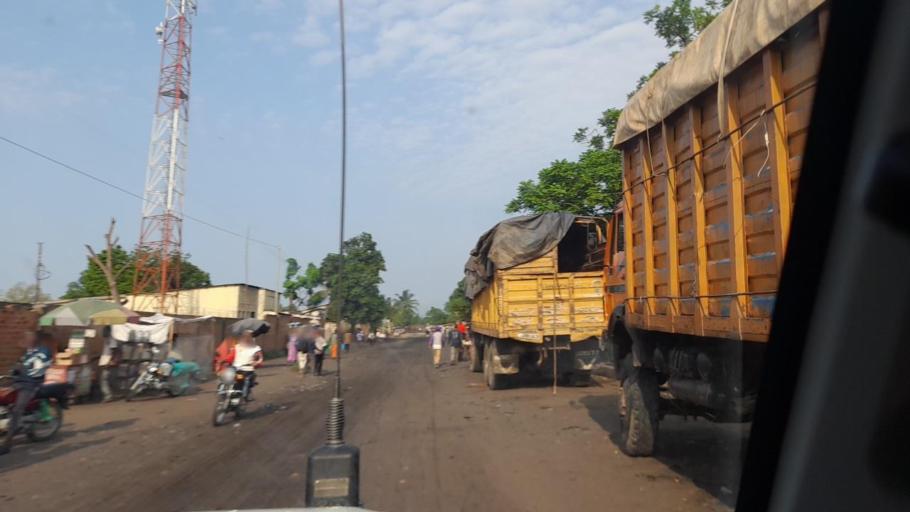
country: CD
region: Kasai-Occidental
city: Kananga
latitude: -5.8951
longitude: 22.3911
